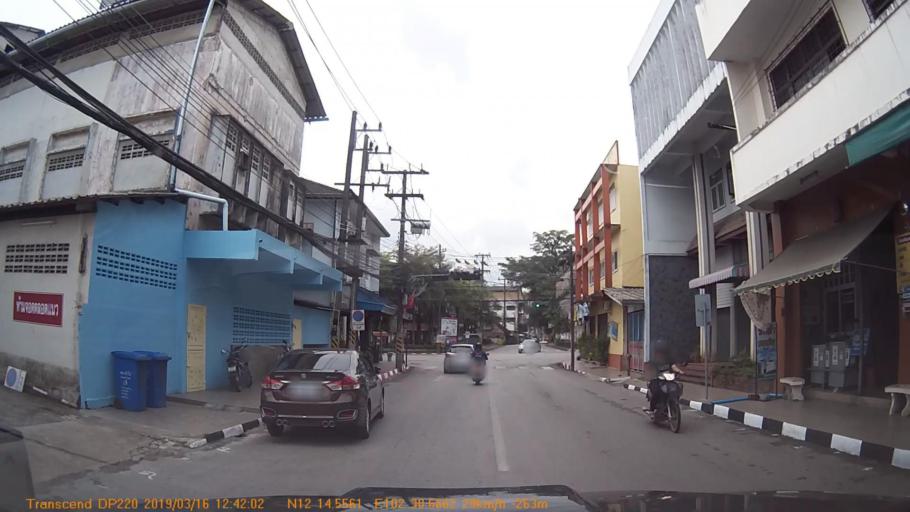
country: TH
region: Trat
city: Trat
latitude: 12.2426
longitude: 102.5110
